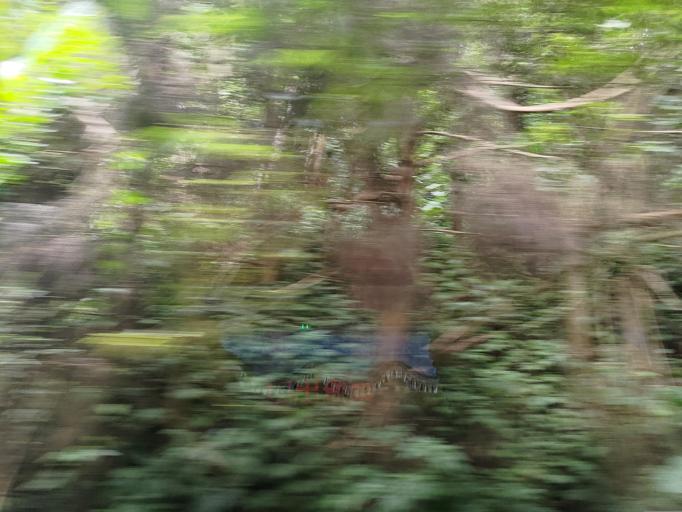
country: TW
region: Taiwan
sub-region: Hsinchu
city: Hsinchu
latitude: 24.6219
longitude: 121.0433
